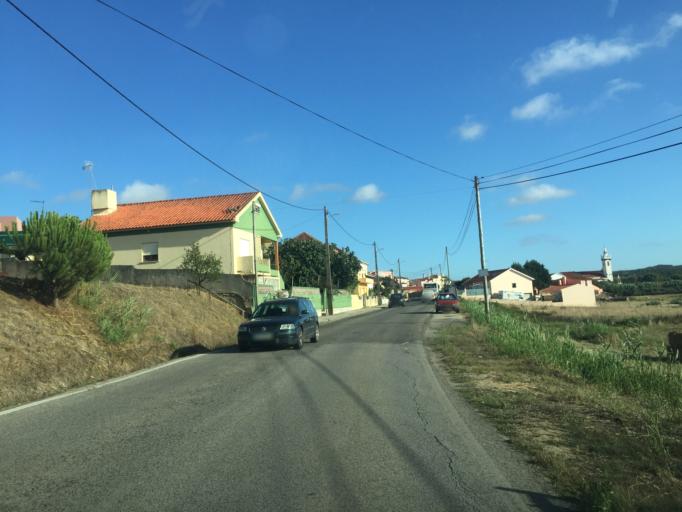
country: PT
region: Lisbon
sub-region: Torres Vedras
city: A dos Cunhados
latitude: 39.1561
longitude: -9.2998
